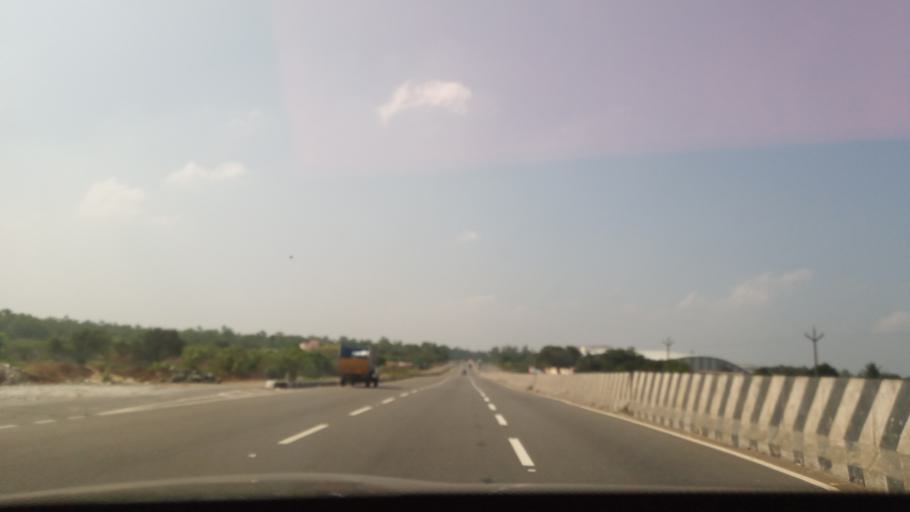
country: IN
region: Tamil Nadu
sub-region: Kancheepuram
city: Madambakkam
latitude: 12.8655
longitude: 79.9656
